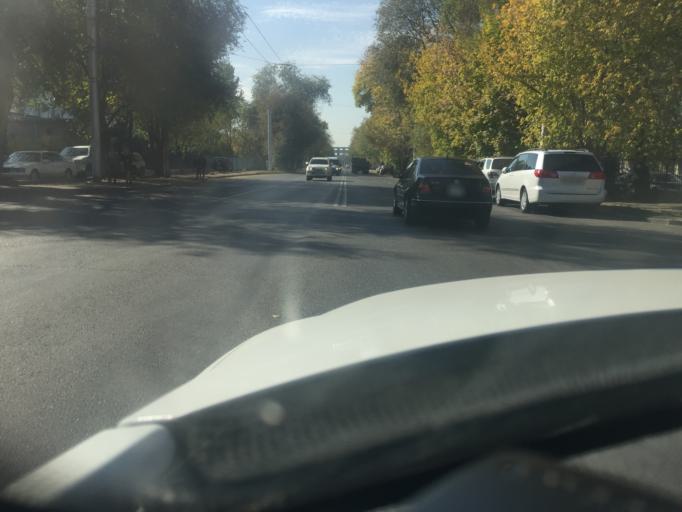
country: KZ
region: Almaty Qalasy
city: Almaty
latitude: 43.2575
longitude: 76.9095
